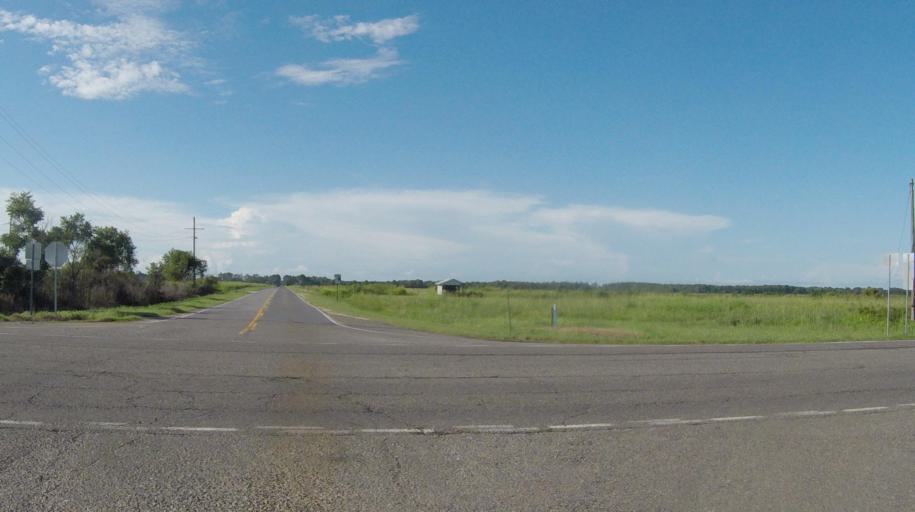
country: US
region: Louisiana
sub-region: Allen Parish
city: Kinder
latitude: 30.4818
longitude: -92.7745
